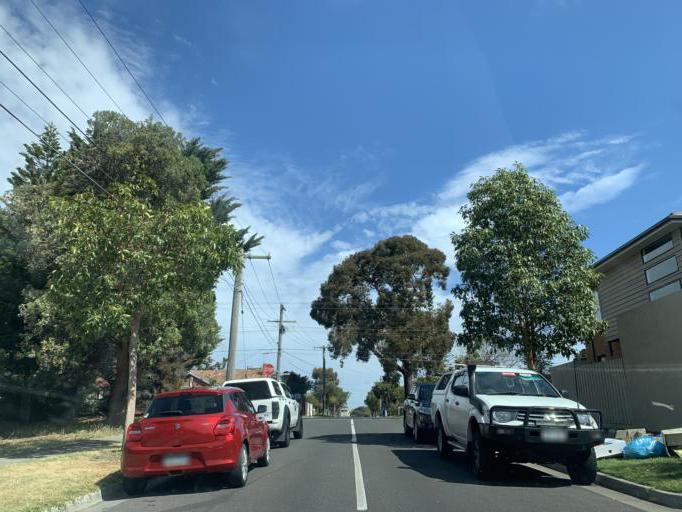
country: AU
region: Victoria
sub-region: Bayside
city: Hampton East
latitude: -37.9430
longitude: 145.0281
